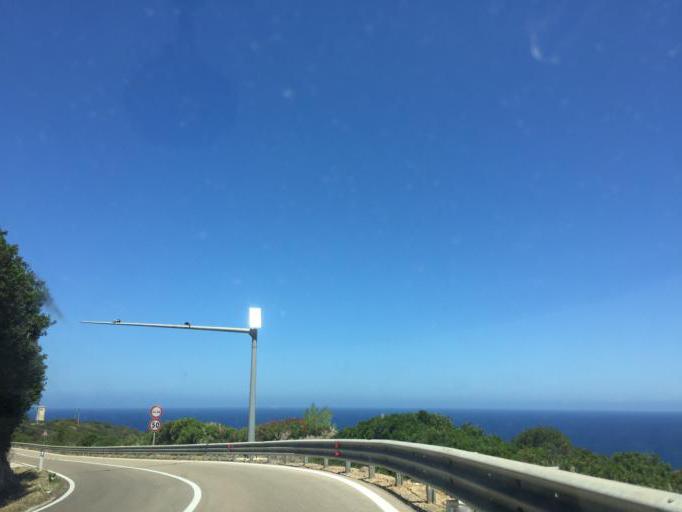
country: IT
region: Sardinia
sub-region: Provincia di Sassari
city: Castelsardo
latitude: 40.9096
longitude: 8.7376
